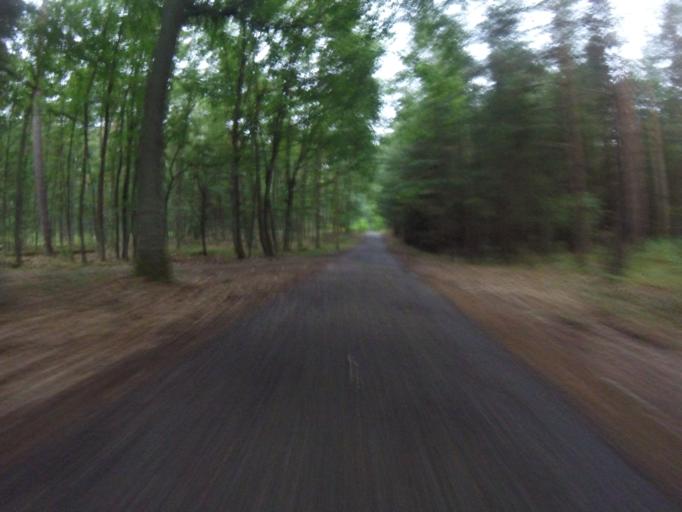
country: DE
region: Brandenburg
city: Gross Koris
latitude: 52.2160
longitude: 13.7043
